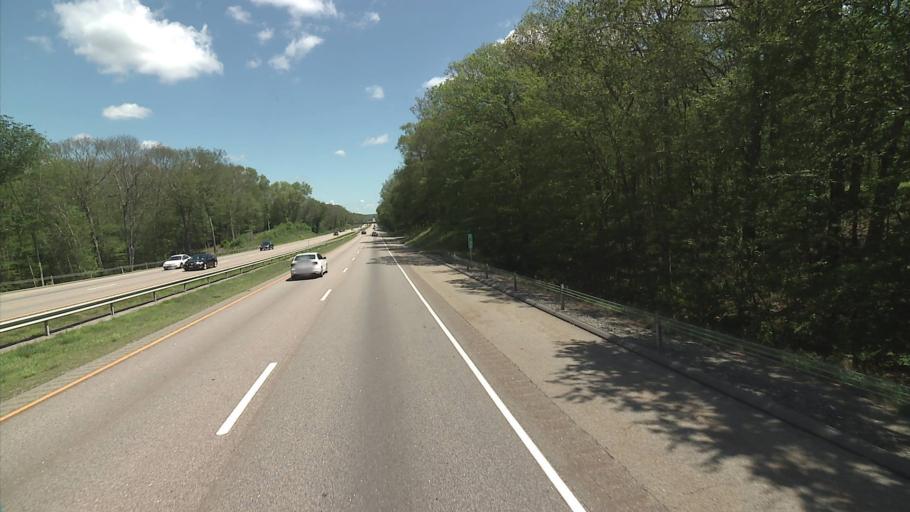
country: US
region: Connecticut
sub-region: New London County
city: Oxoboxo River
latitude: 41.4078
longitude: -72.1452
